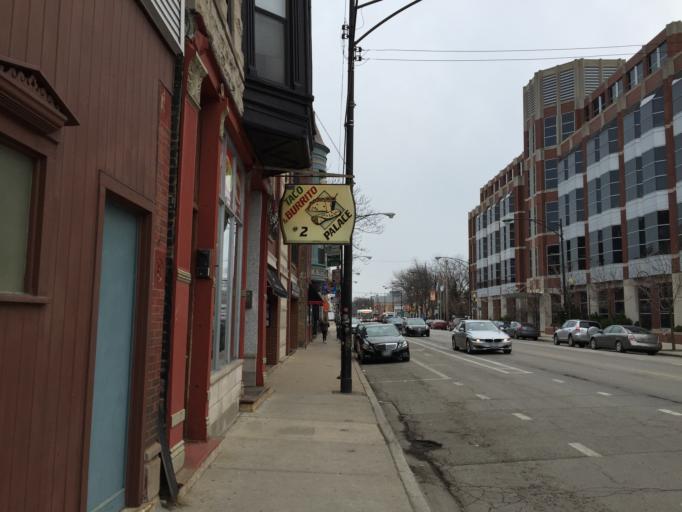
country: US
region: Illinois
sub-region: Cook County
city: Chicago
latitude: 41.9273
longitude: -87.6488
